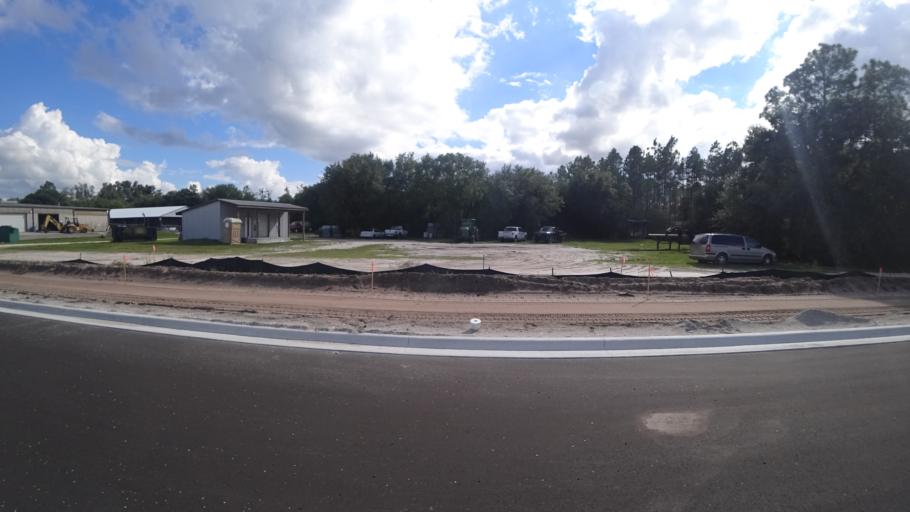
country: US
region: Florida
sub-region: Sarasota County
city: The Meadows
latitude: 27.4553
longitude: -82.3975
